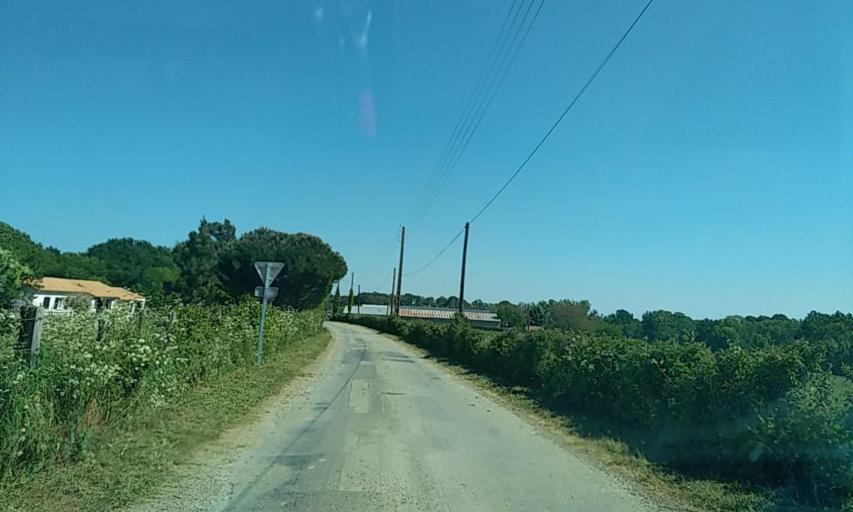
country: FR
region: Poitou-Charentes
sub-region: Departement des Deux-Sevres
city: La Chapelle-Saint-Laurent
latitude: 46.7866
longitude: -0.4780
